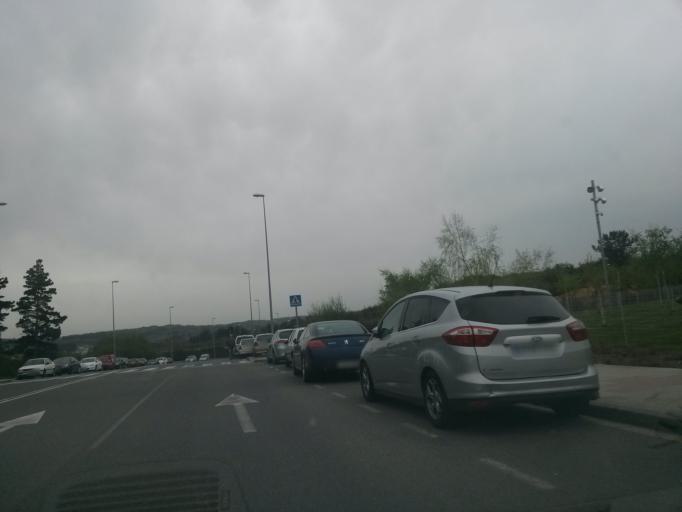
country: ES
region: Galicia
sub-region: Provincia de Lugo
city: Lugo
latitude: 43.0224
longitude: -7.5354
